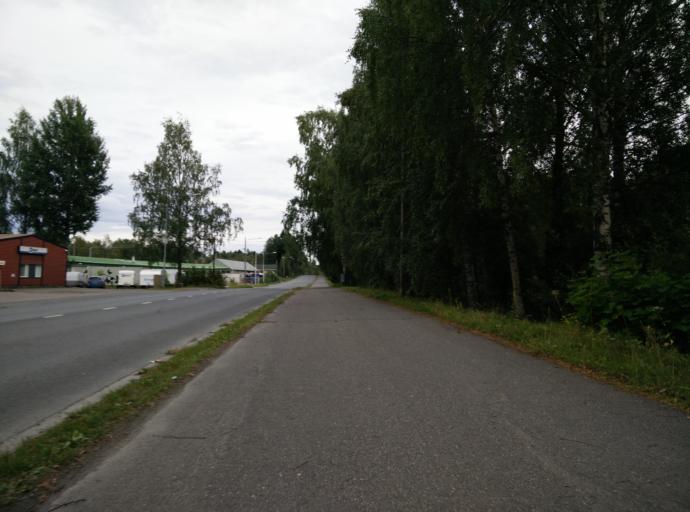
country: FI
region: Haeme
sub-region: Haemeenlinna
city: Haemeenlinna
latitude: 60.9921
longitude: 24.4917
